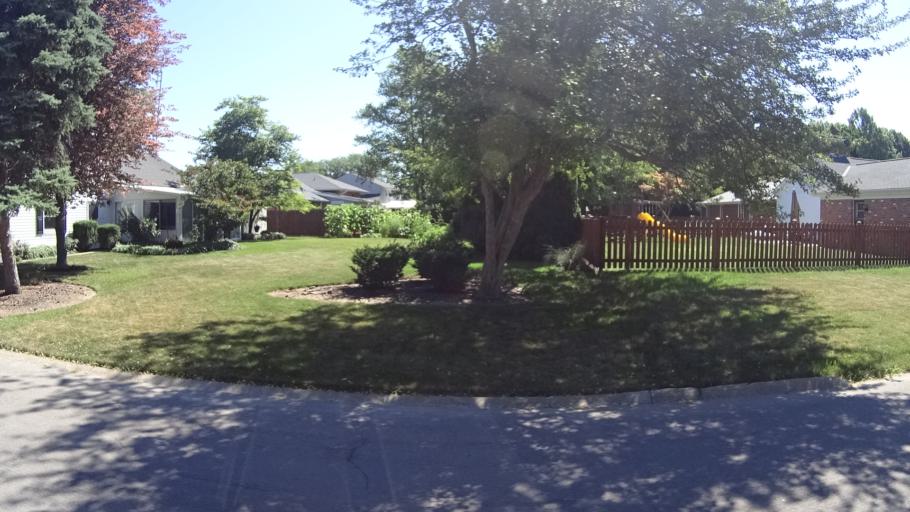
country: US
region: Ohio
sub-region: Erie County
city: Sandusky
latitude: 41.4200
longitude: -82.6961
